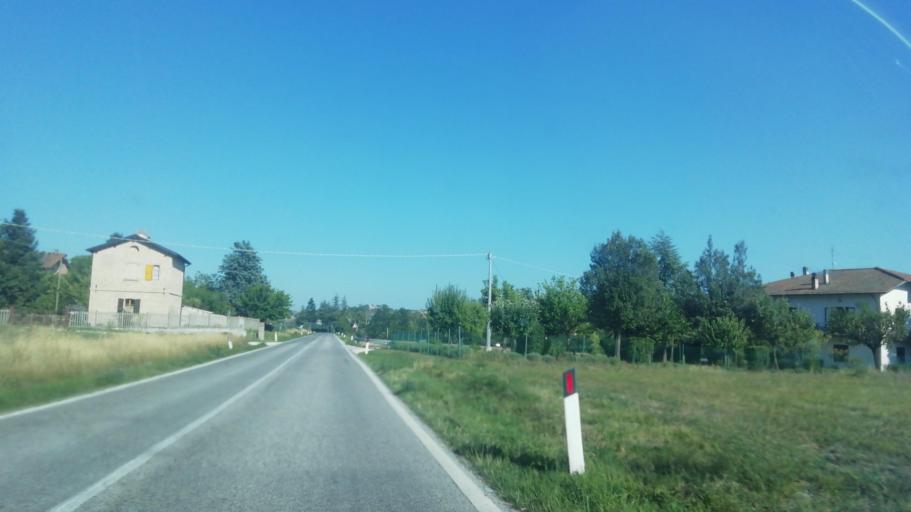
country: IT
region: The Marches
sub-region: Provincia di Pesaro e Urbino
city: Pergola
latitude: 43.5474
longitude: 12.7847
